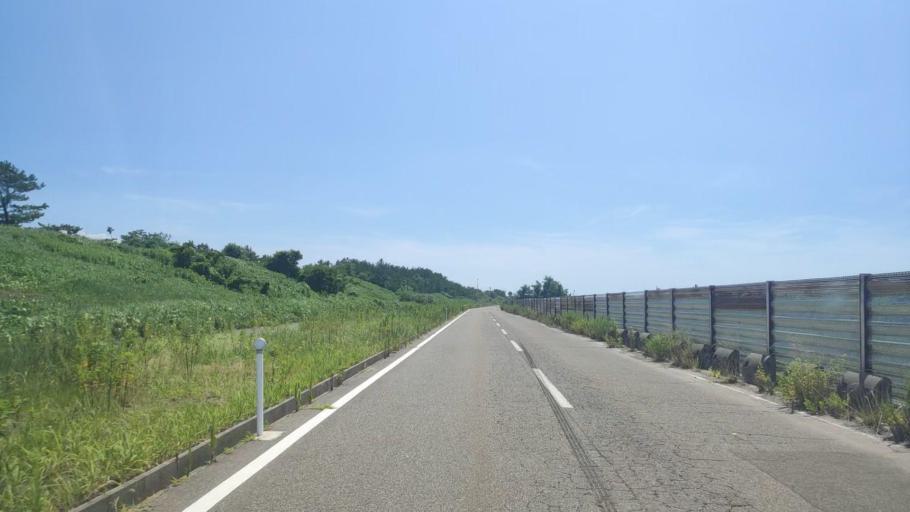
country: JP
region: Ishikawa
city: Kanazawa-shi
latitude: 36.6111
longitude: 136.5969
